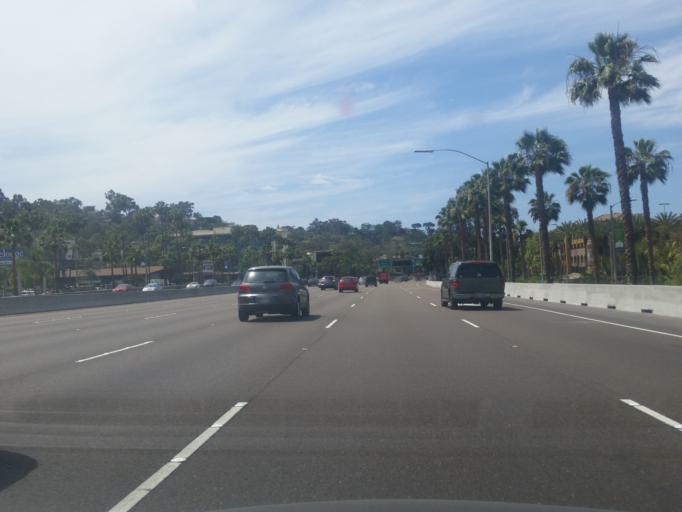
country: US
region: California
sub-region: San Diego County
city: San Diego
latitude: 32.7601
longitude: -117.1727
